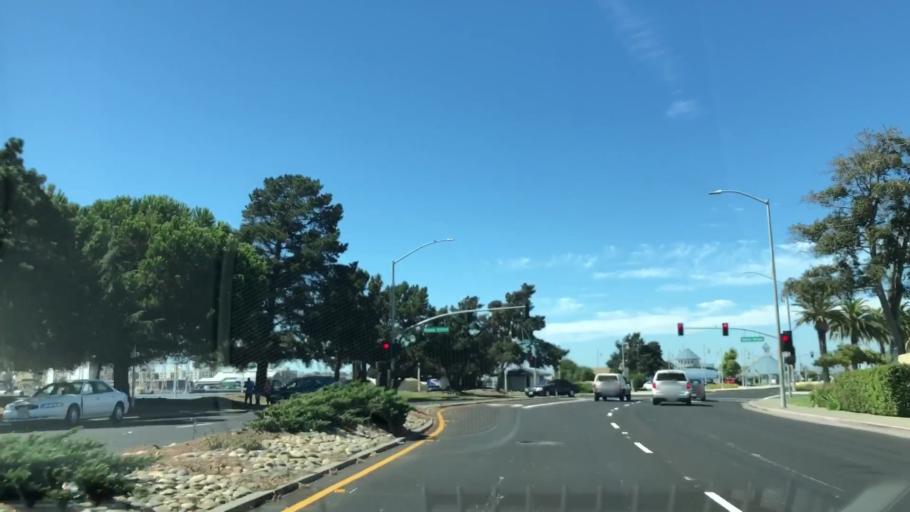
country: US
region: California
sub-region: Solano County
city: Vallejo
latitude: 38.0983
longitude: -122.2608
